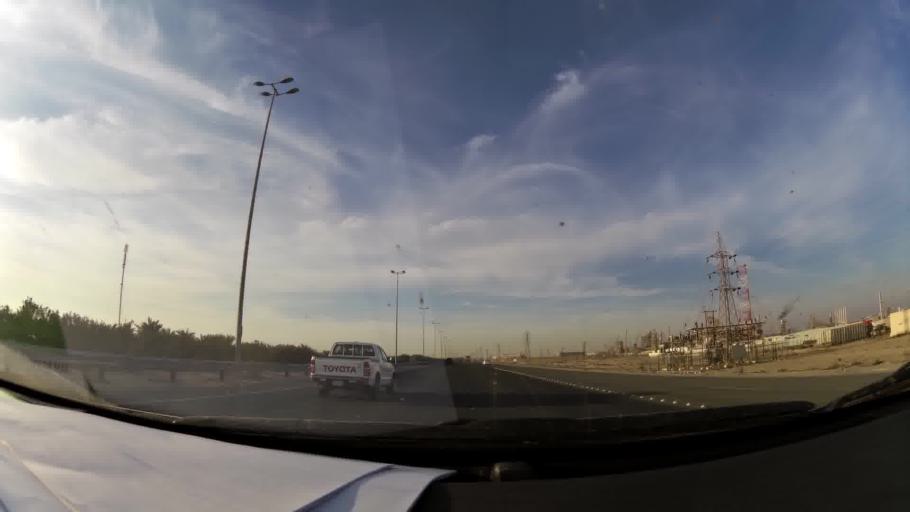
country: KW
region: Al Ahmadi
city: Al Fahahil
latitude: 28.9867
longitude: 48.1506
